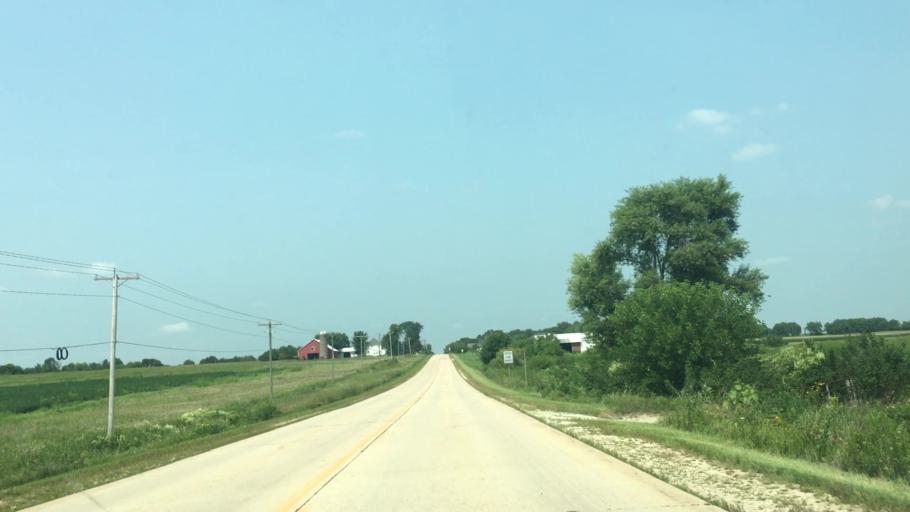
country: US
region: Iowa
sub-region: Fayette County
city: Oelwein
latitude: 42.6698
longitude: -91.8937
